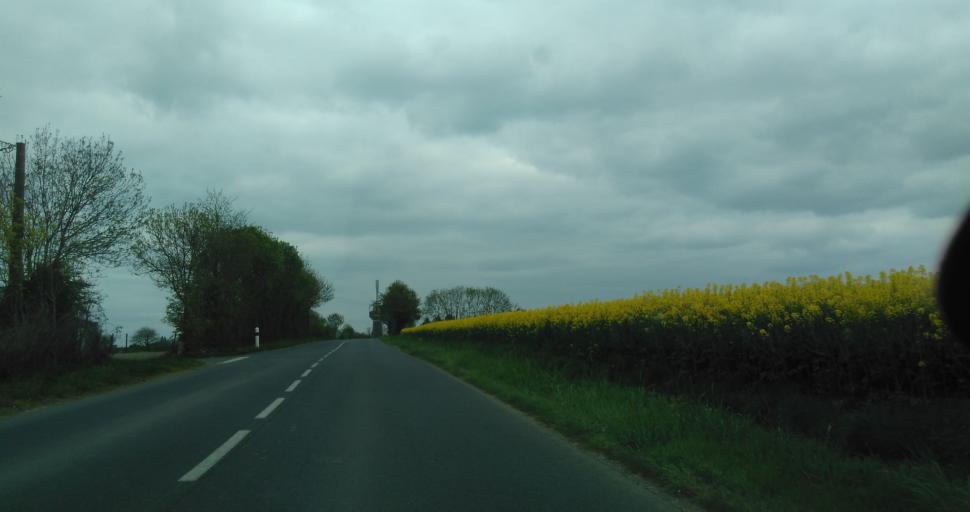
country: FR
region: Poitou-Charentes
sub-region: Departement des Deux-Sevres
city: La Chapelle-Saint-Laurent
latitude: 46.7359
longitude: -0.4875
